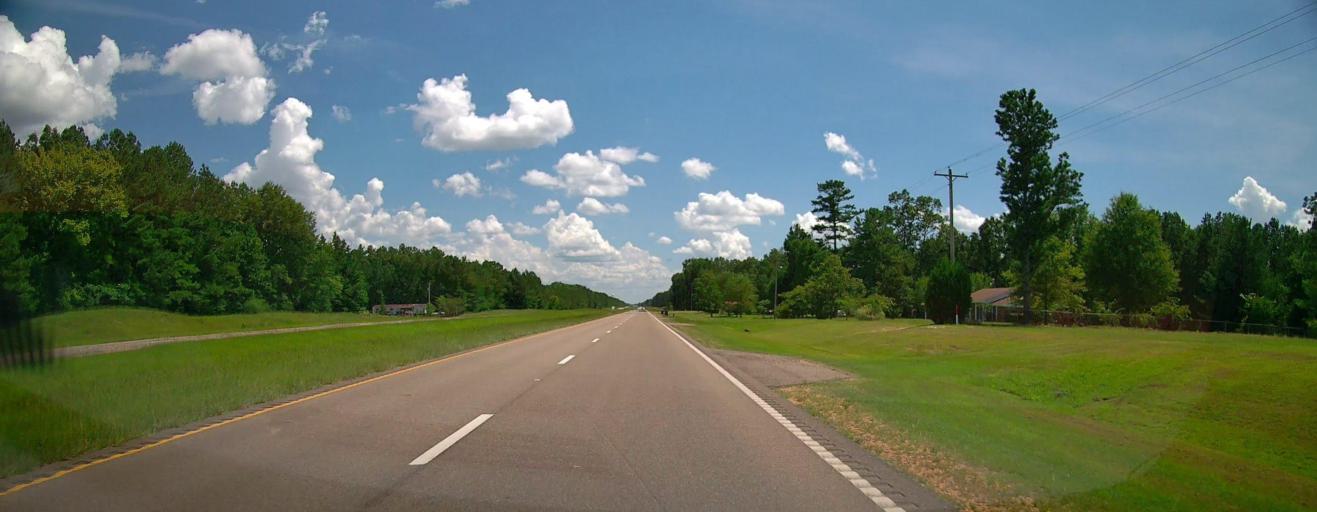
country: US
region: Mississippi
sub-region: Monroe County
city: Aberdeen
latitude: 33.9242
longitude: -88.5962
